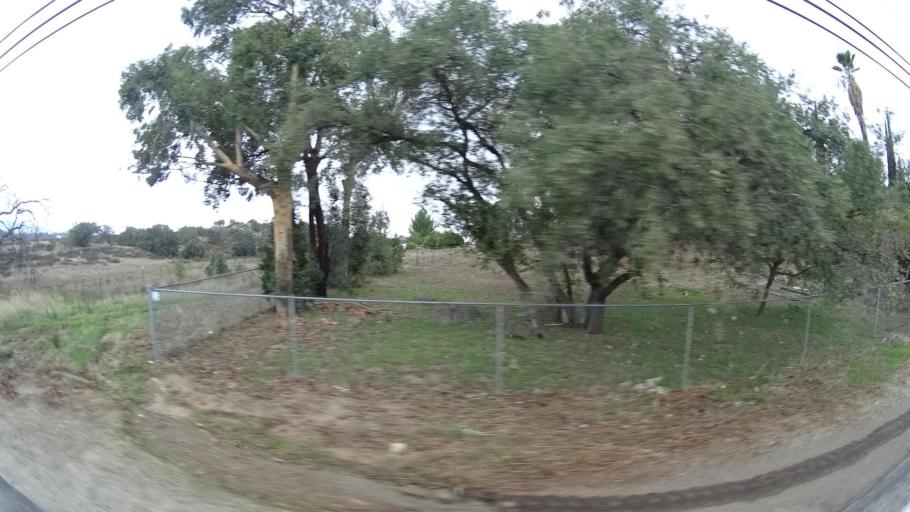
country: US
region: California
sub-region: San Diego County
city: Alpine
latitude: 32.8230
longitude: -116.7585
